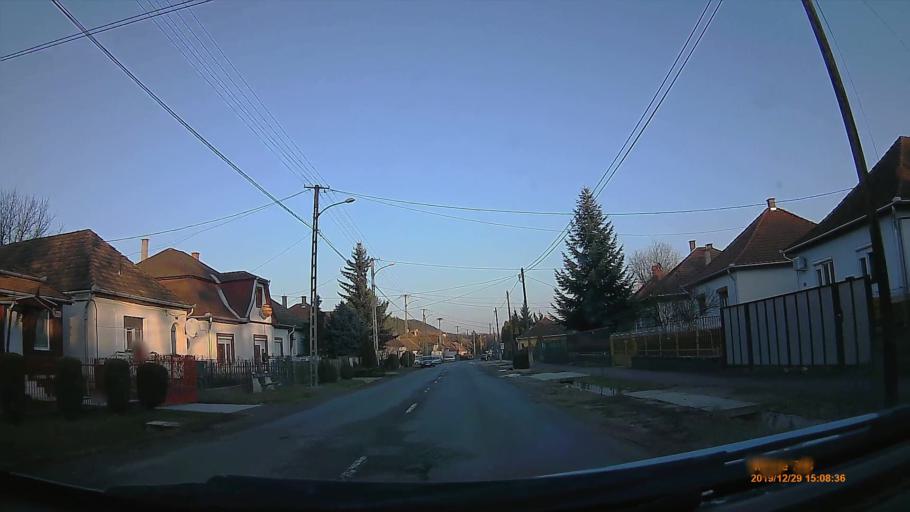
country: HU
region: Heves
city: Parad
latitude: 47.9235
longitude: 20.0407
